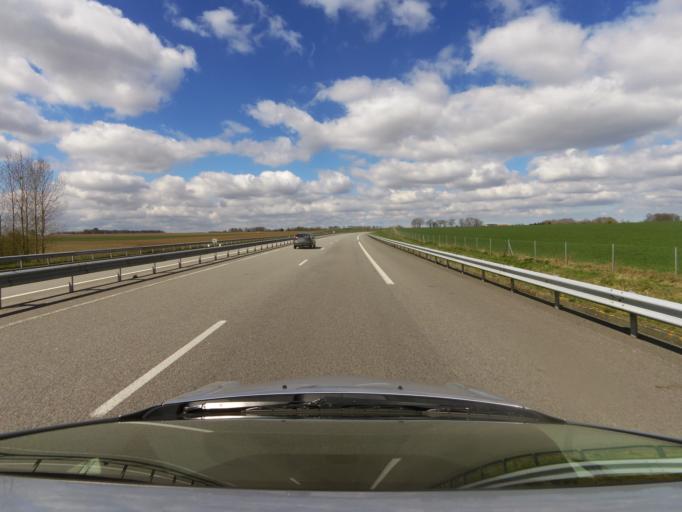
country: FR
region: Haute-Normandie
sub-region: Departement de la Seine-Maritime
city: Limesy
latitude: 49.6490
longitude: 0.9575
